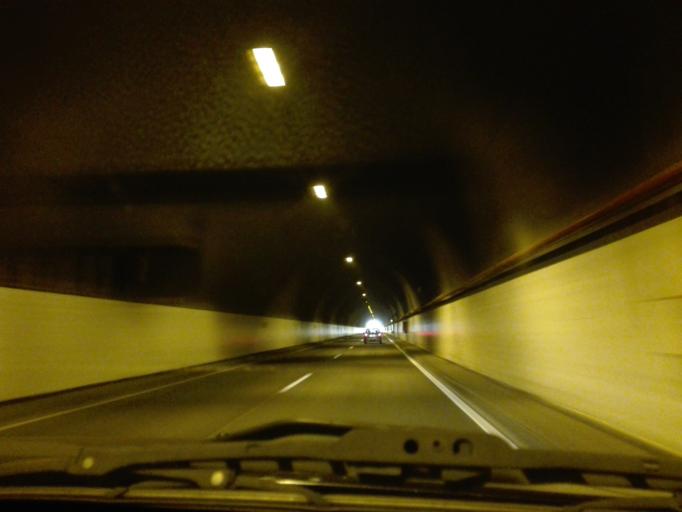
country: PT
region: Madeira
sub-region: Machico
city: Machico
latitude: 32.7345
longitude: -16.7995
